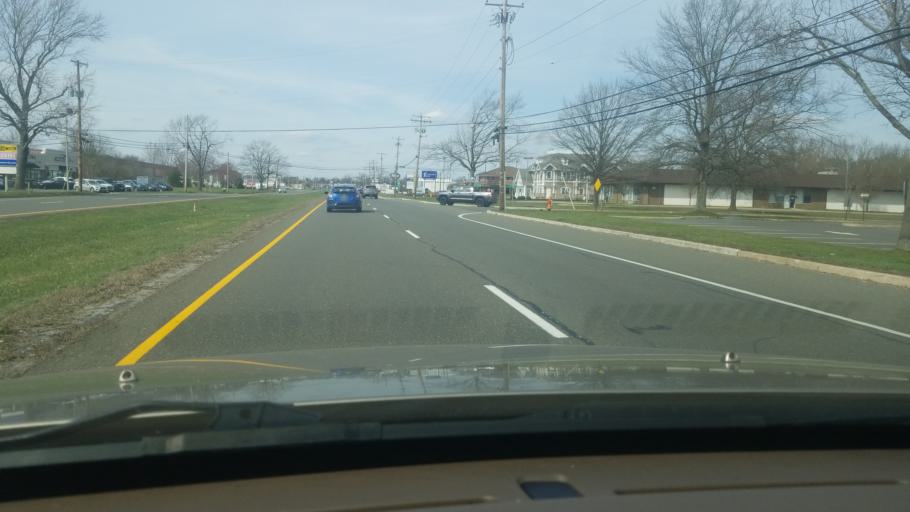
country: US
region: New Jersey
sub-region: Monmouth County
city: Freehold
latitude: 40.2287
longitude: -74.2721
